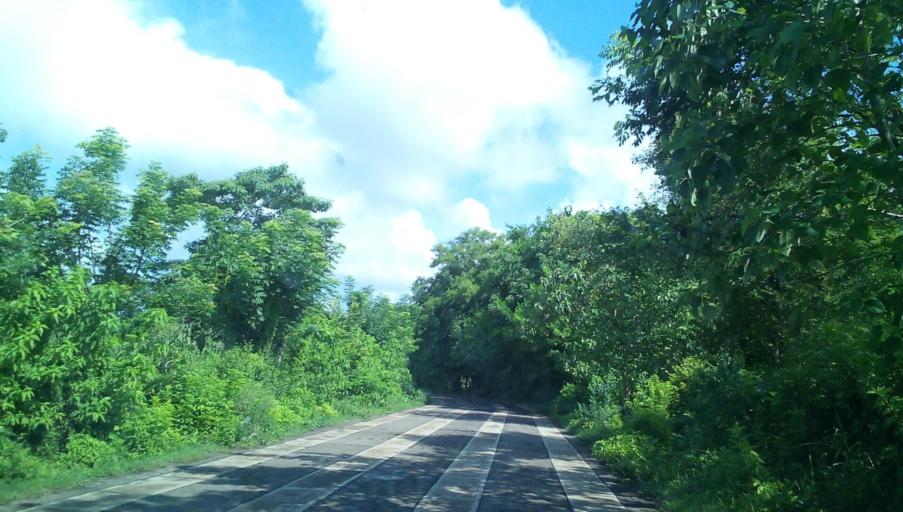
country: MX
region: Veracruz
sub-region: Citlaltepetl
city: Las Sabinas
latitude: 21.3489
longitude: -97.8943
